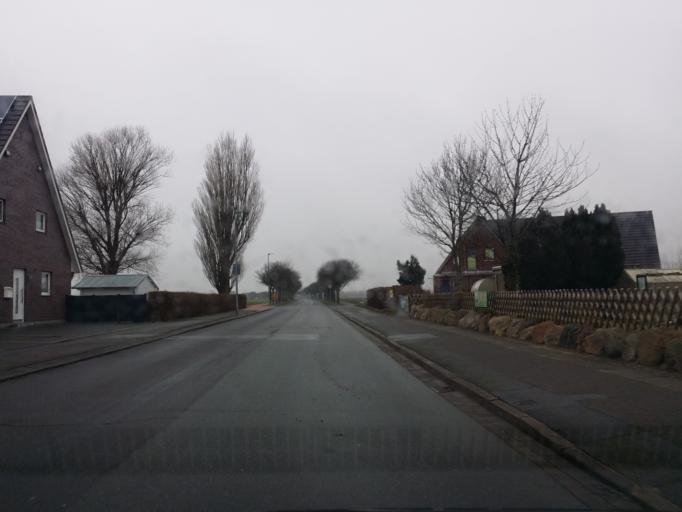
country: DE
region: Schleswig-Holstein
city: Burg auf Fehmarn
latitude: 54.4231
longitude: 11.2069
